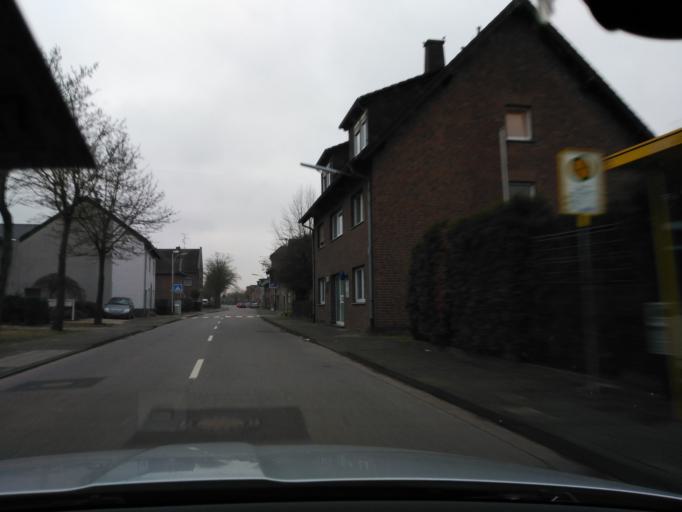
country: DE
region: North Rhine-Westphalia
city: Wegberg
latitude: 51.1325
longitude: 6.3083
